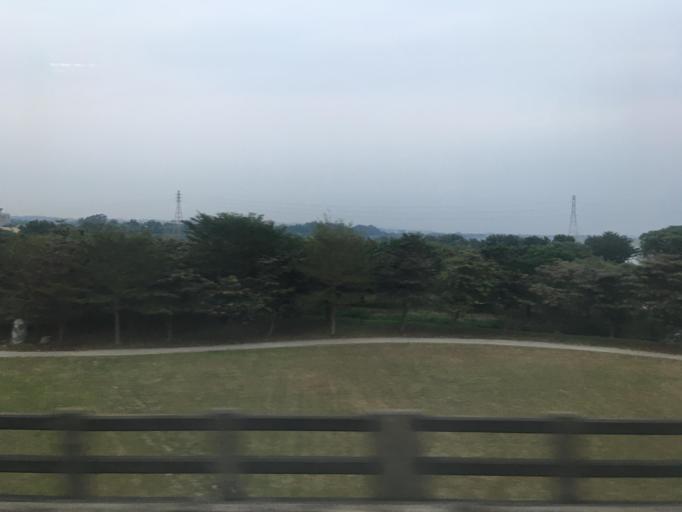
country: TW
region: Taiwan
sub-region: Pingtung
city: Pingtung
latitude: 22.6624
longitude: 120.4292
